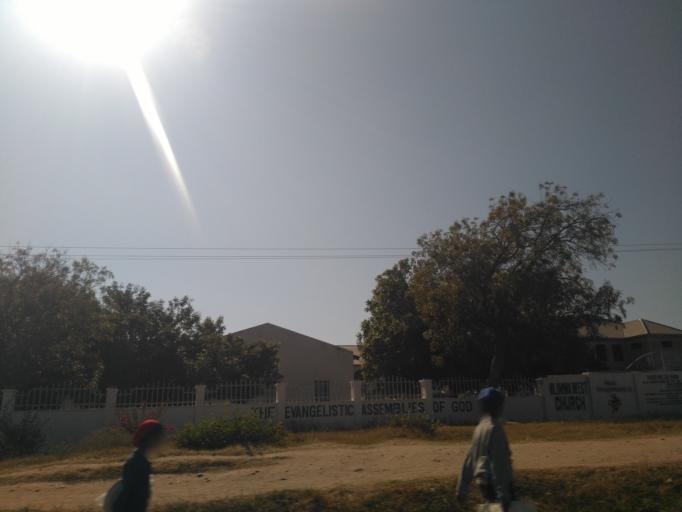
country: TZ
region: Dodoma
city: Dodoma
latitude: -6.1561
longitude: 35.7469
